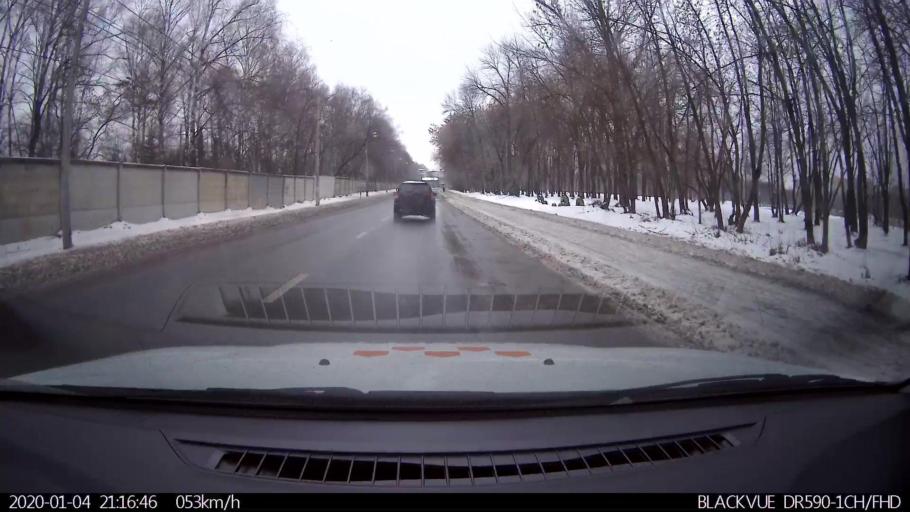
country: RU
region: Nizjnij Novgorod
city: Gorbatovka
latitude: 56.2386
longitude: 43.8499
